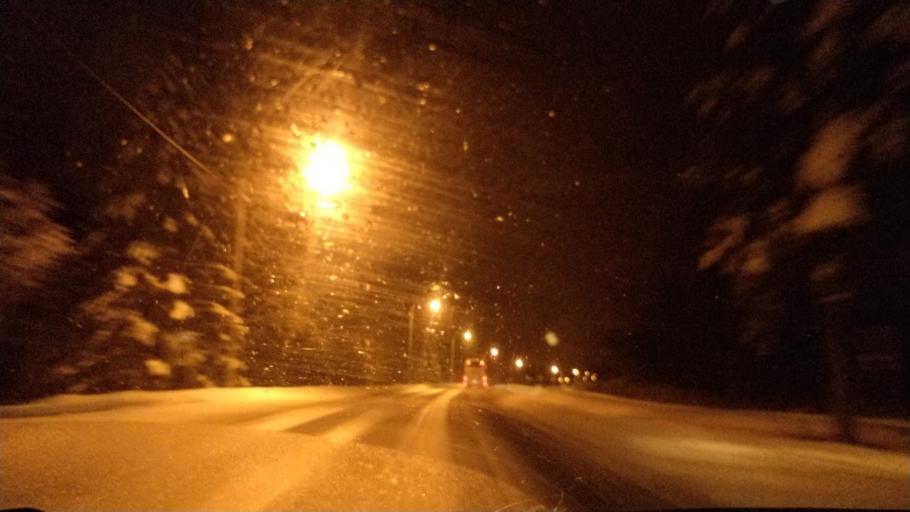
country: FI
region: Lapland
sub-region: Rovaniemi
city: Rovaniemi
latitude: 66.2900
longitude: 25.3488
